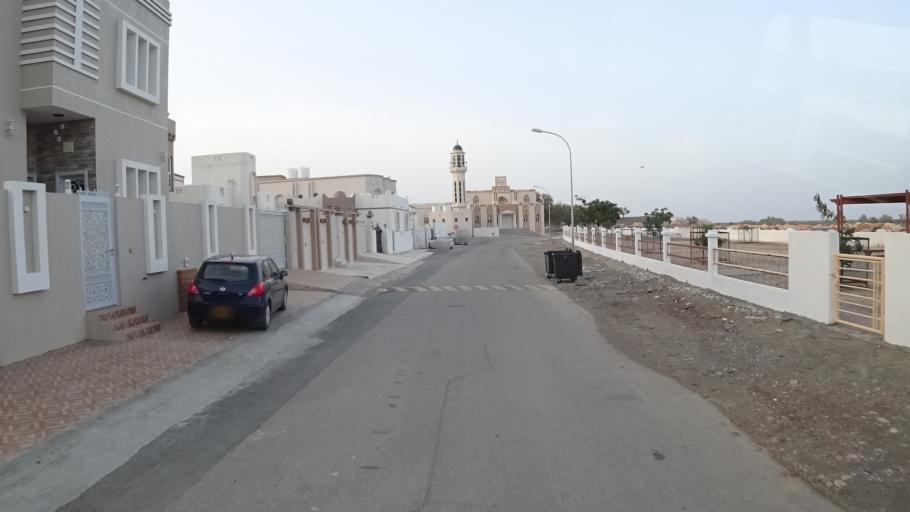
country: OM
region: Muhafazat Masqat
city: Muscat
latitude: 23.2150
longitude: 58.9738
